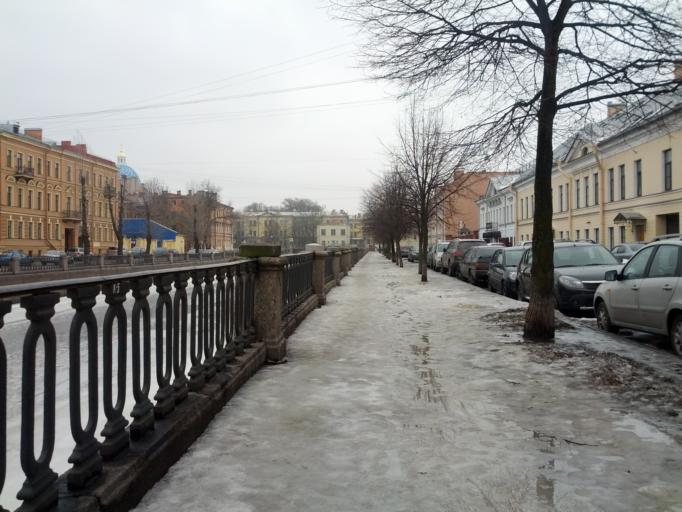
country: RU
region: St.-Petersburg
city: Admiralteisky
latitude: 59.9198
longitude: 30.2995
